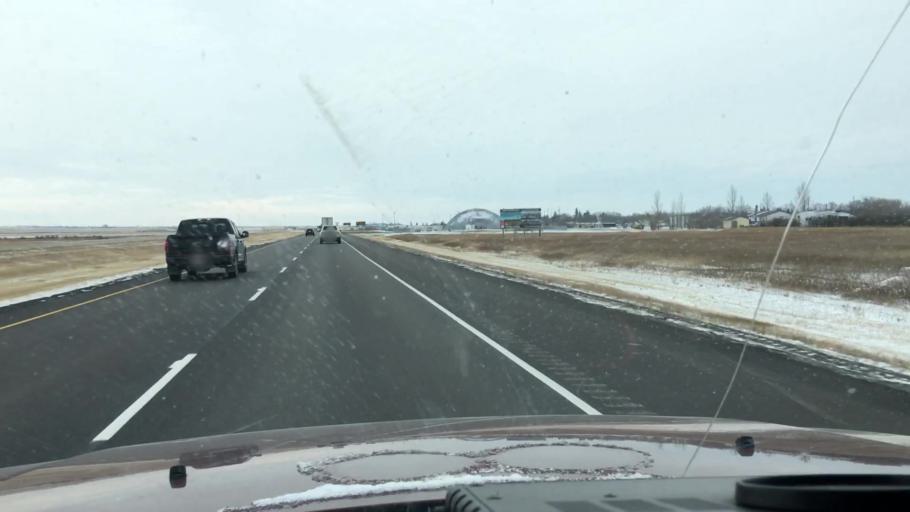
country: CA
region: Saskatchewan
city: Saskatoon
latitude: 51.8201
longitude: -106.4993
